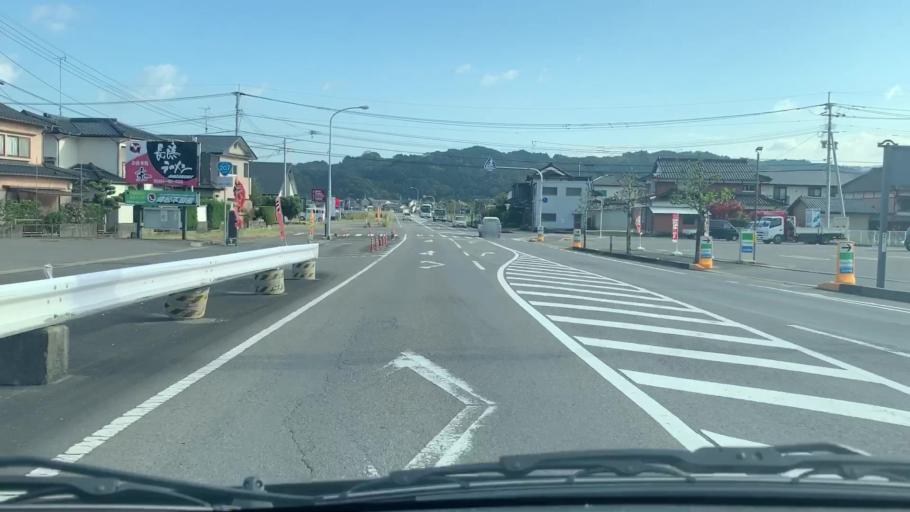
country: JP
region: Saga Prefecture
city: Kashima
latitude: 33.0939
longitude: 130.0942
